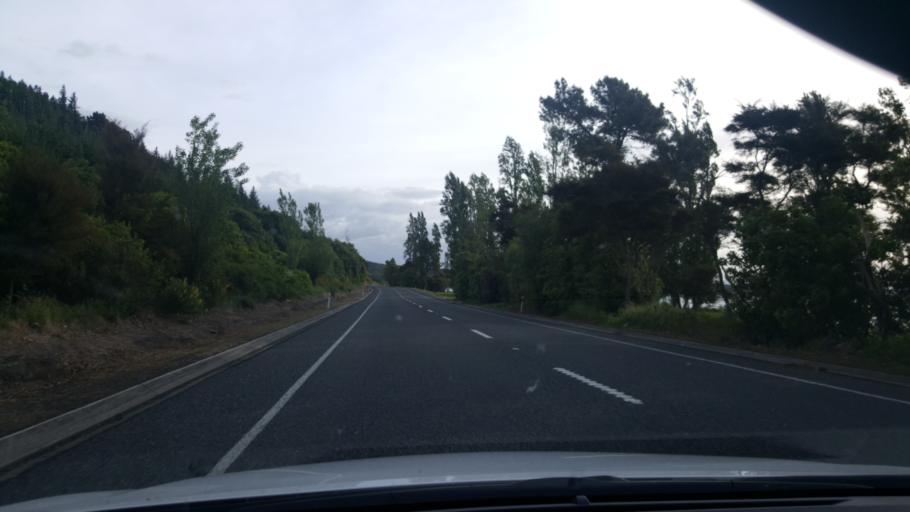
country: NZ
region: Waikato
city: Turangi
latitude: -38.8928
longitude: 175.9490
